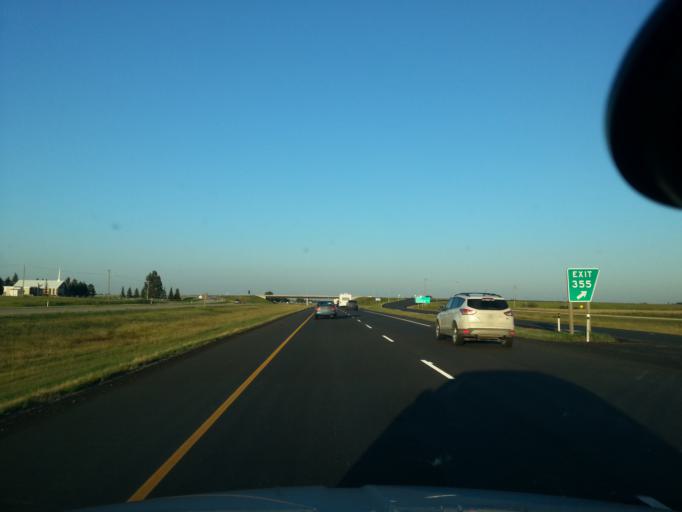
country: CA
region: Alberta
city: Stony Plain
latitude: 53.5694
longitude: -114.0087
